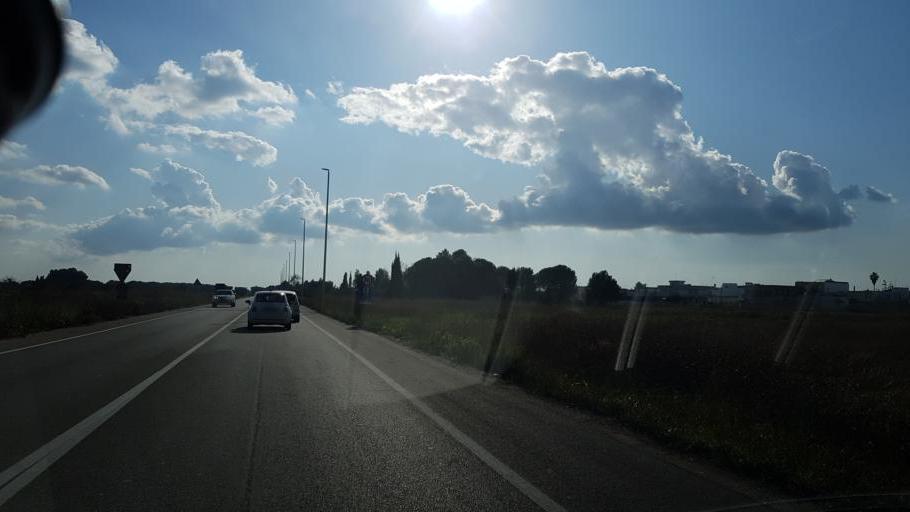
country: IT
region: Apulia
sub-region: Provincia di Lecce
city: Salice Salentino
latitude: 40.3798
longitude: 17.9698
